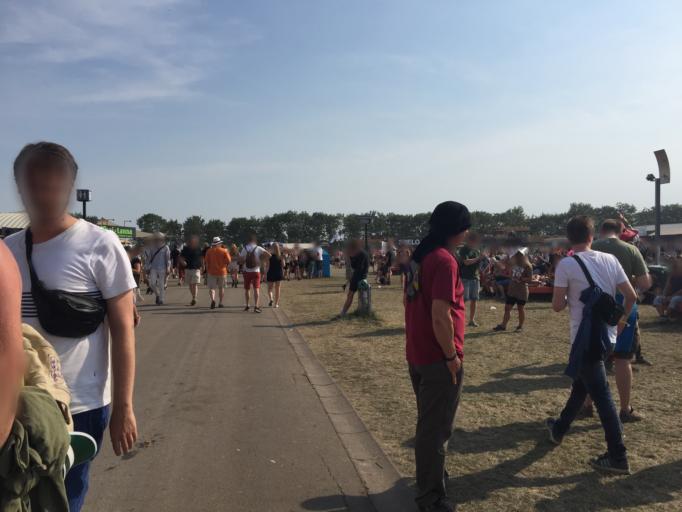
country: DK
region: Zealand
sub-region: Roskilde Kommune
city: Roskilde
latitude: 55.6207
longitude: 12.0790
